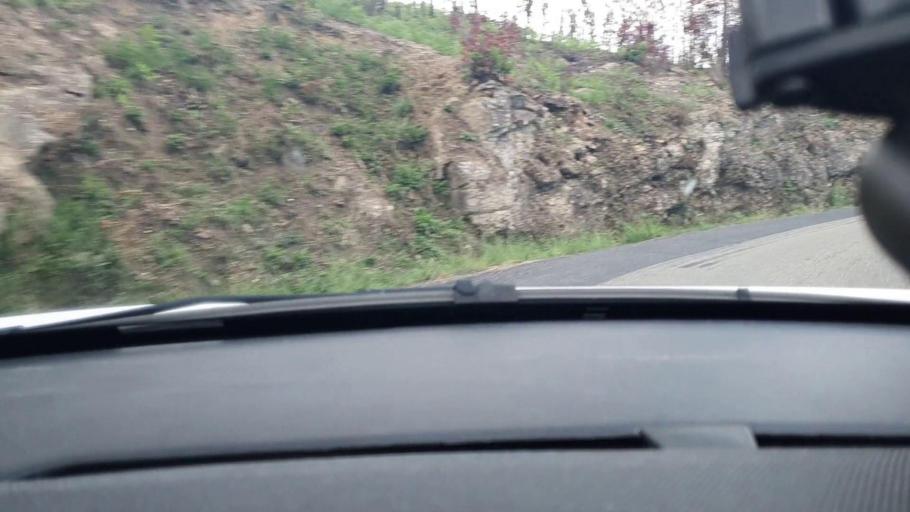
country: FR
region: Languedoc-Roussillon
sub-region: Departement du Gard
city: Besseges
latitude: 44.3238
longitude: 4.0854
